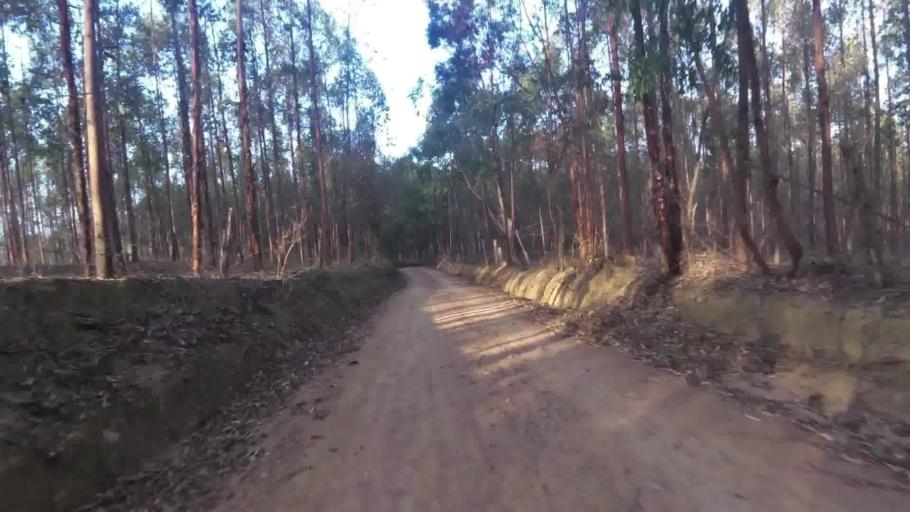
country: BR
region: Espirito Santo
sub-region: Marataizes
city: Marataizes
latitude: -21.1628
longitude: -41.0405
